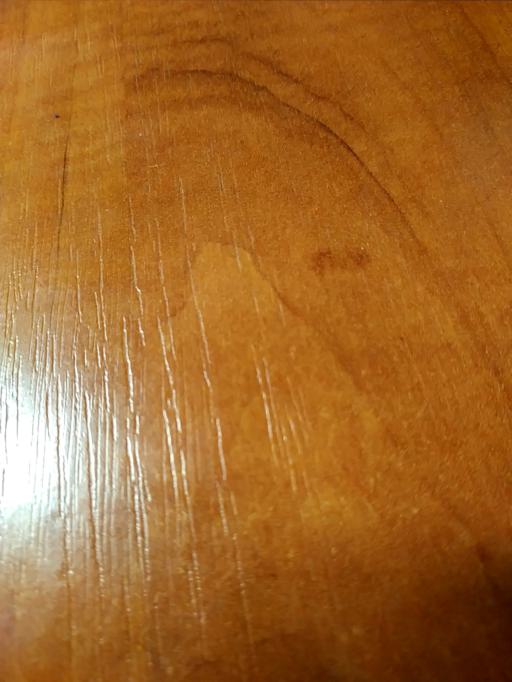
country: RU
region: Lipetsk
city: Chaplygin
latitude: 53.3347
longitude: 40.0569
